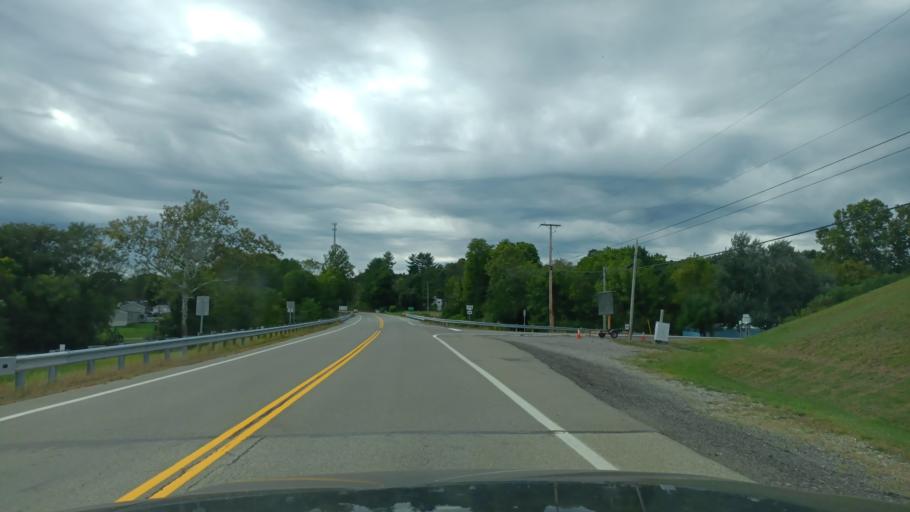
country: US
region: Ohio
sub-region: Vinton County
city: McArthur
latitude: 39.2390
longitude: -82.3854
